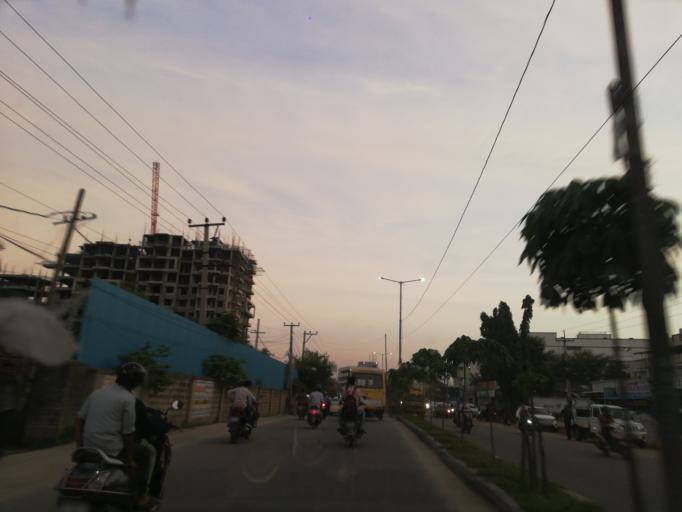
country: IN
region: Telangana
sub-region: Rangareddi
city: Kukatpalli
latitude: 17.5051
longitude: 78.3623
